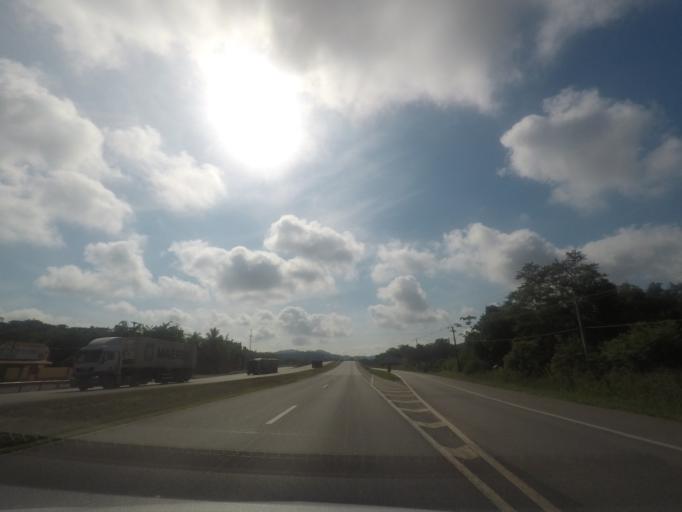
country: BR
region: Parana
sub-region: Antonina
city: Antonina
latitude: -25.5497
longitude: -48.7947
